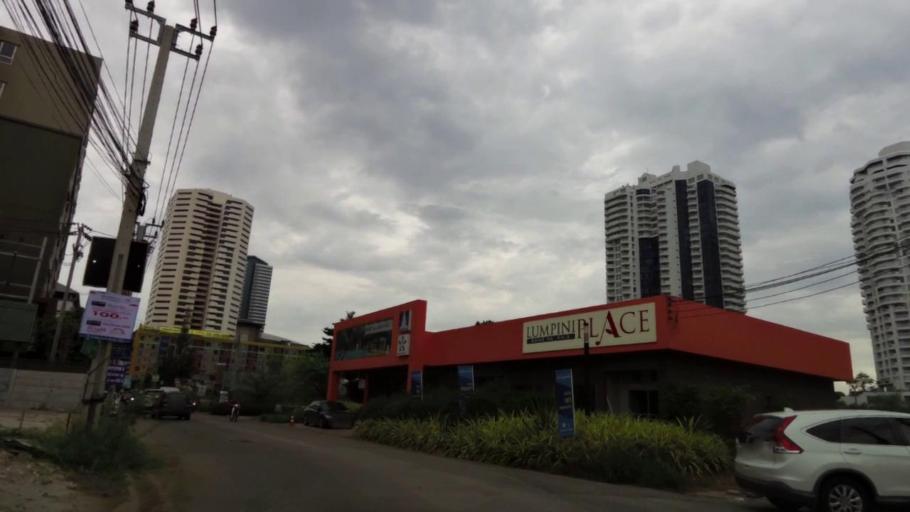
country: TH
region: Bangkok
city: Bang Na
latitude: 13.6737
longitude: 100.6367
